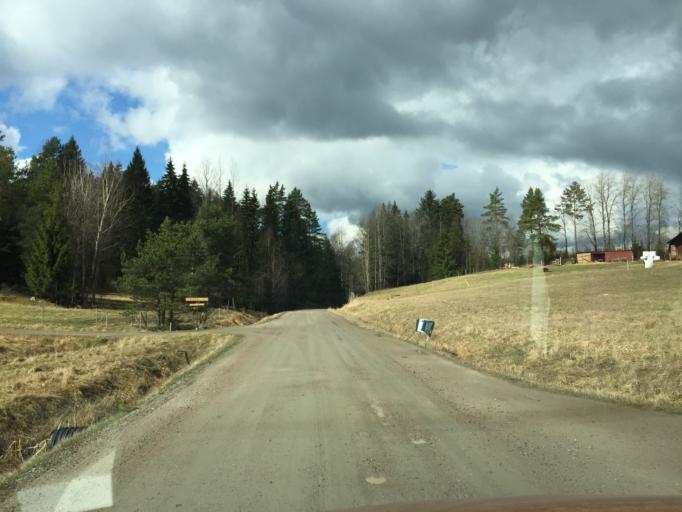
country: SE
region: Soedermanland
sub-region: Nykopings Kommun
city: Nykoping
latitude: 58.9606
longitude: 17.0478
